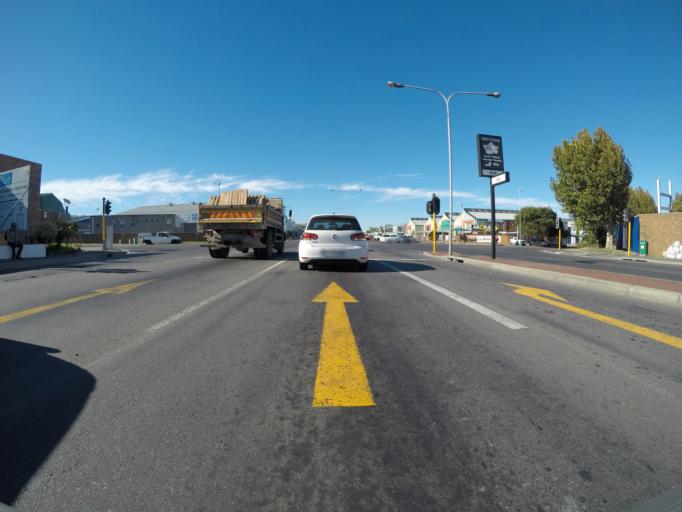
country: ZA
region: Western Cape
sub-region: City of Cape Town
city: Kraaifontein
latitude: -33.9036
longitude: 18.6685
